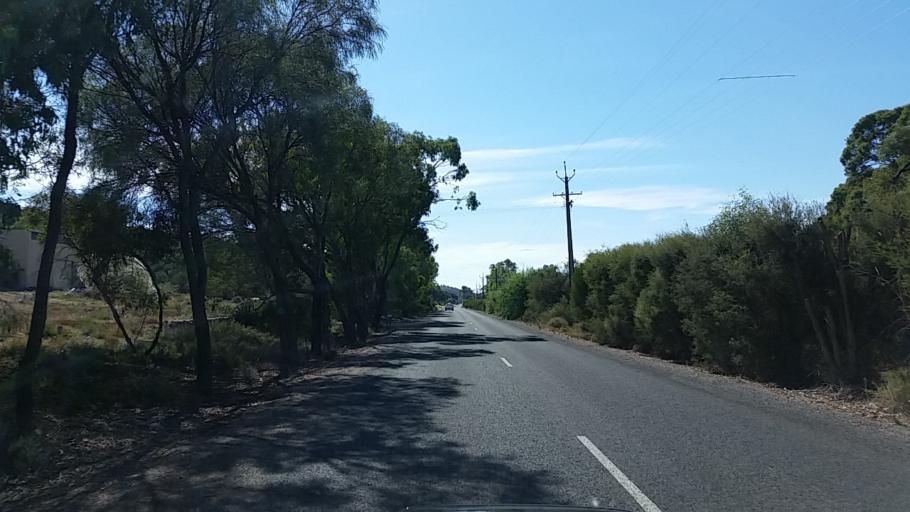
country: AU
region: South Australia
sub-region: Mid Murray
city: Mannum
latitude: -34.7080
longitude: 139.5659
